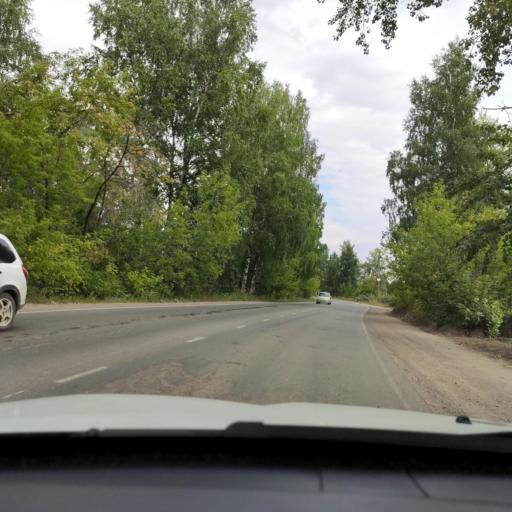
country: RU
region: Perm
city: Krasnokamsk
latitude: 58.0835
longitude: 55.7894
